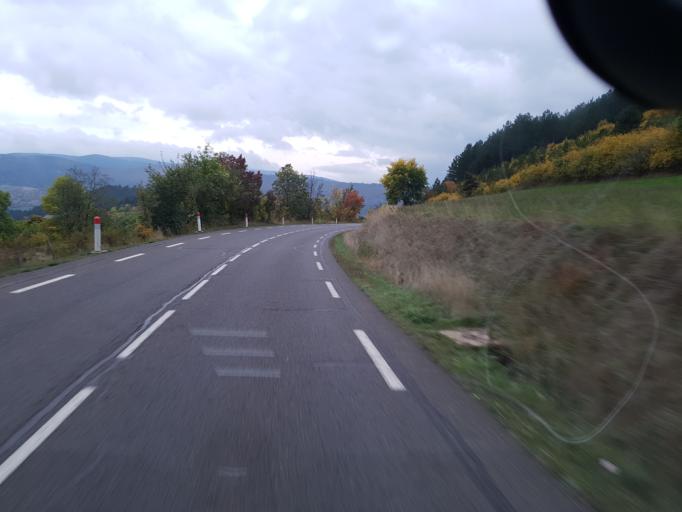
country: FR
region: Languedoc-Roussillon
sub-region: Departement de la Lozere
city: Mende
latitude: 44.5440
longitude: 3.6133
